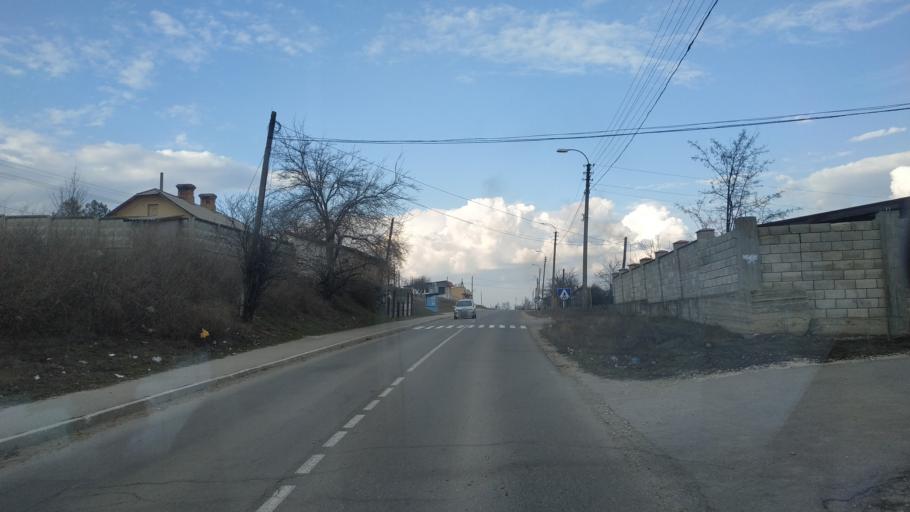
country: MD
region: Anenii Noi
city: Varnita
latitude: 46.8693
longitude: 29.4752
